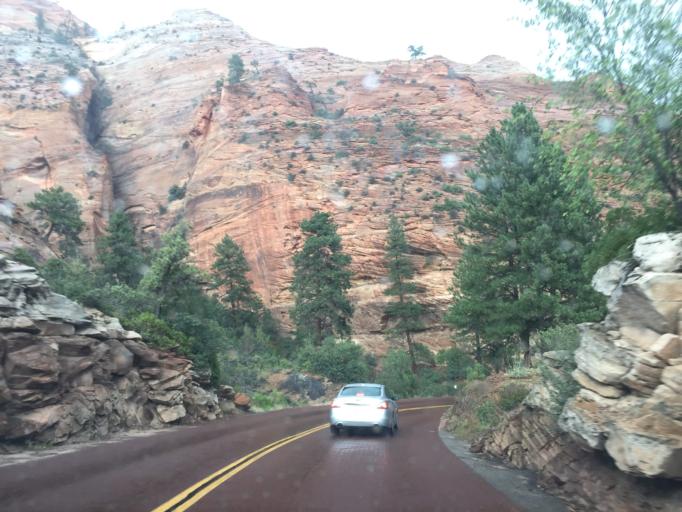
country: US
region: Utah
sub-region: Washington County
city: Hildale
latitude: 37.2169
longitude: -112.9286
